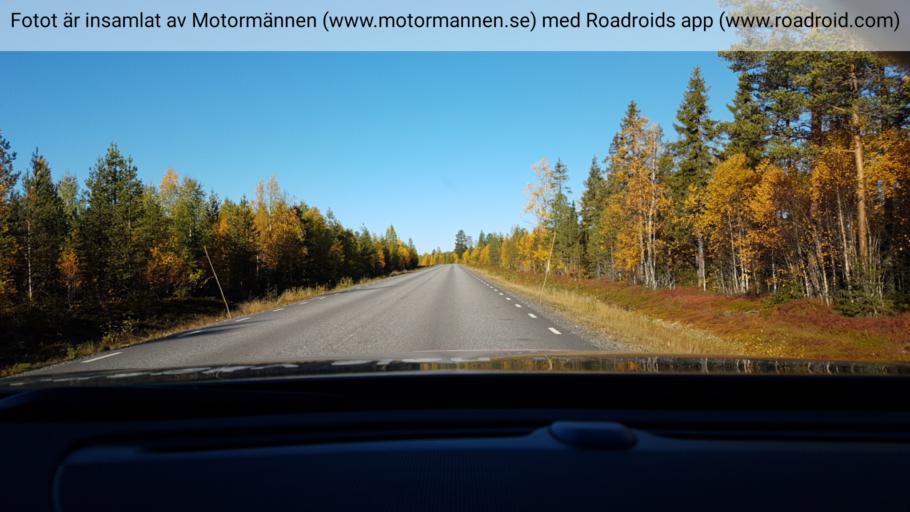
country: SE
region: Vaesterbotten
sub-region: Skelleftea Kommun
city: Storvik
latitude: 65.3280
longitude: 20.6744
